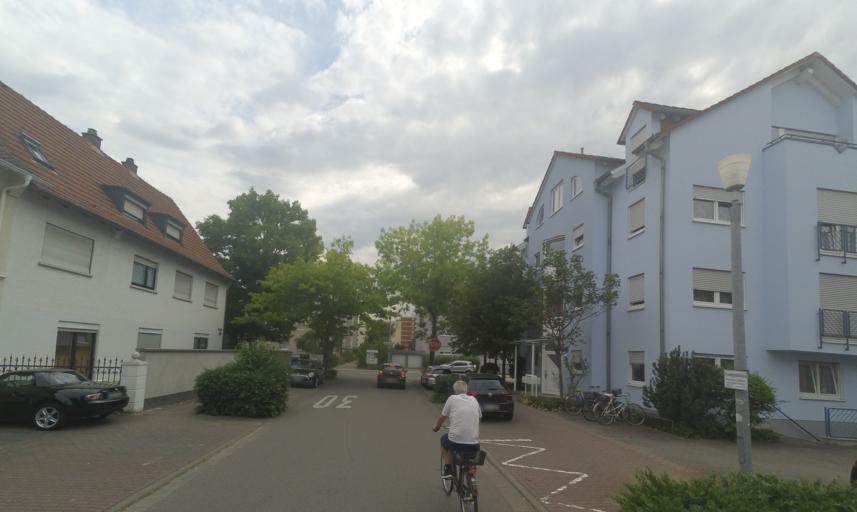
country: DE
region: Hesse
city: Viernheim
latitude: 49.5305
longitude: 8.5713
